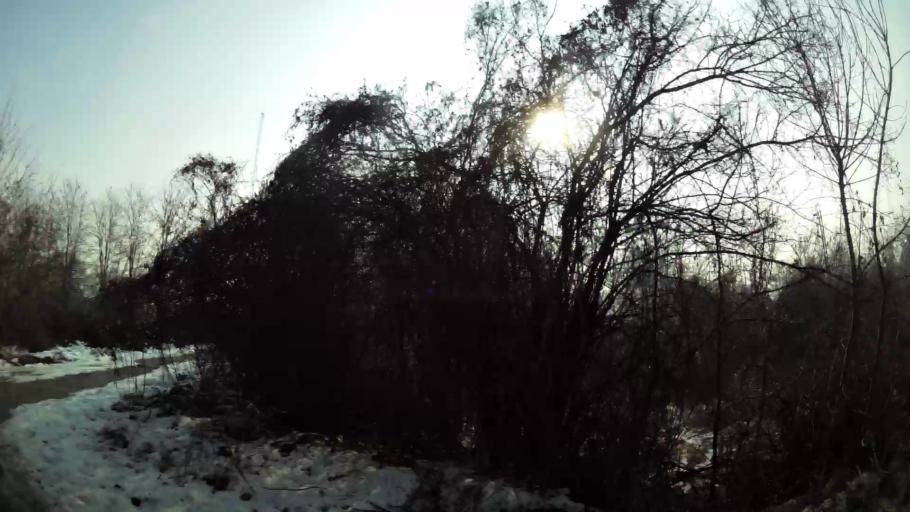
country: MK
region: Ilinden
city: Jurumleri
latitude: 41.9912
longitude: 21.5261
